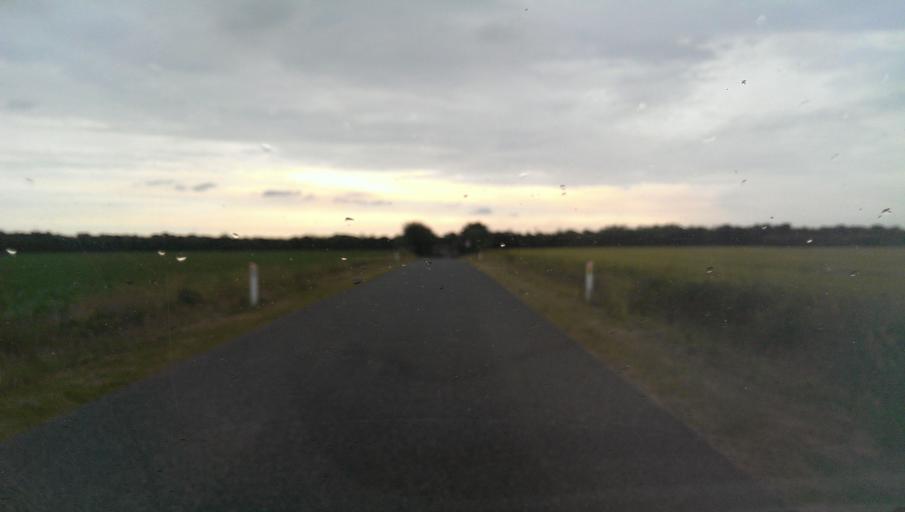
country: DK
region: South Denmark
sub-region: Esbjerg Kommune
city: Bramming
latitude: 55.4356
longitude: 8.6988
